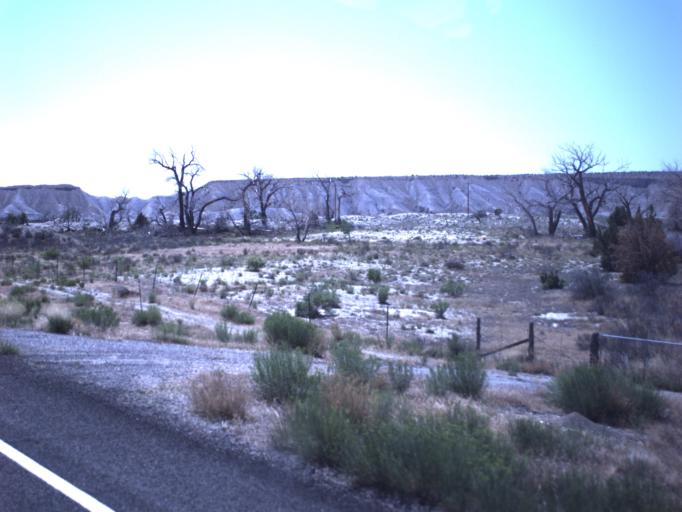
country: US
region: Utah
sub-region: Emery County
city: Orangeville
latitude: 39.2410
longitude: -111.0893
